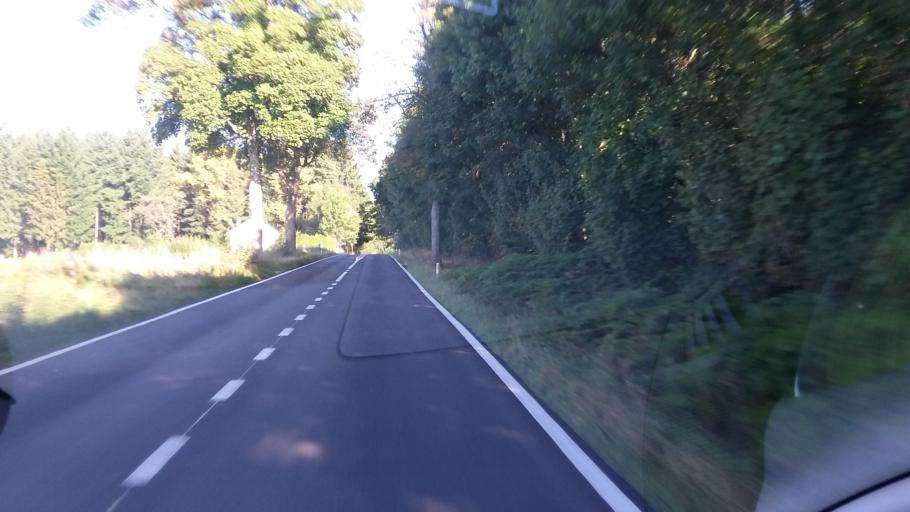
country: BE
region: Wallonia
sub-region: Province du Luxembourg
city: Leglise
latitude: 49.8138
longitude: 5.5032
